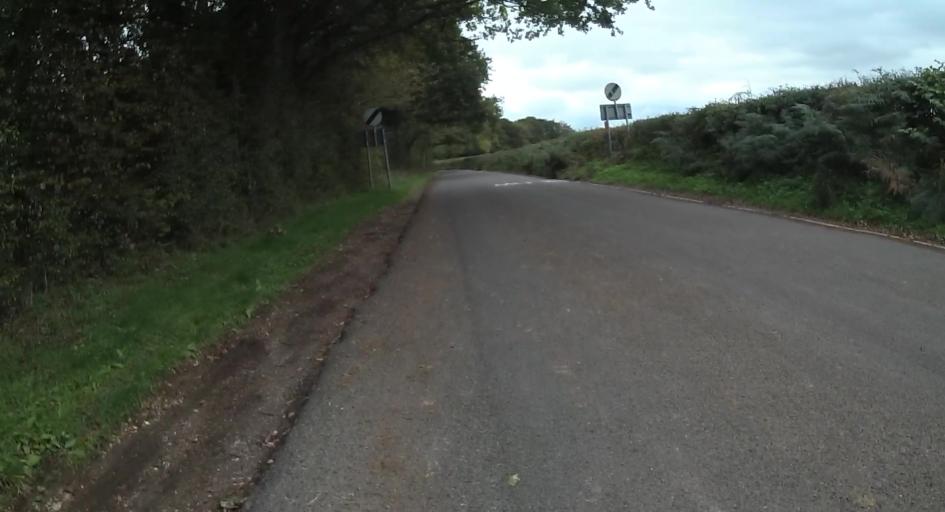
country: GB
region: England
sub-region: Hampshire
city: Four Marks
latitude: 51.0966
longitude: -1.0493
